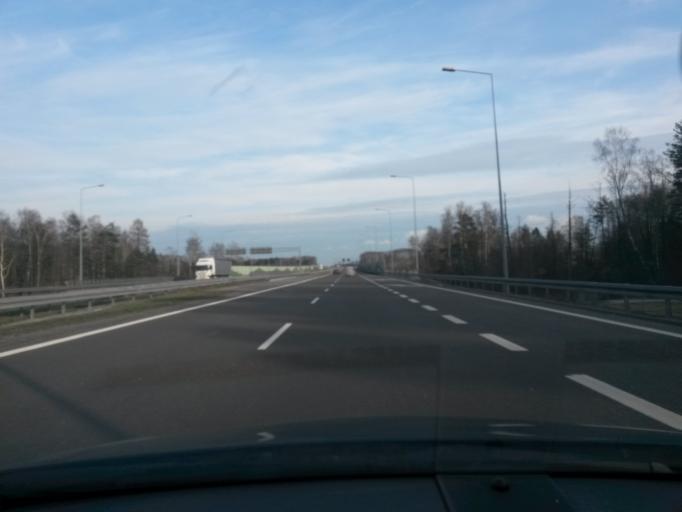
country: PL
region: Lodz Voivodeship
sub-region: Powiat zgierski
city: Zgierz
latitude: 51.9086
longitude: 19.4421
